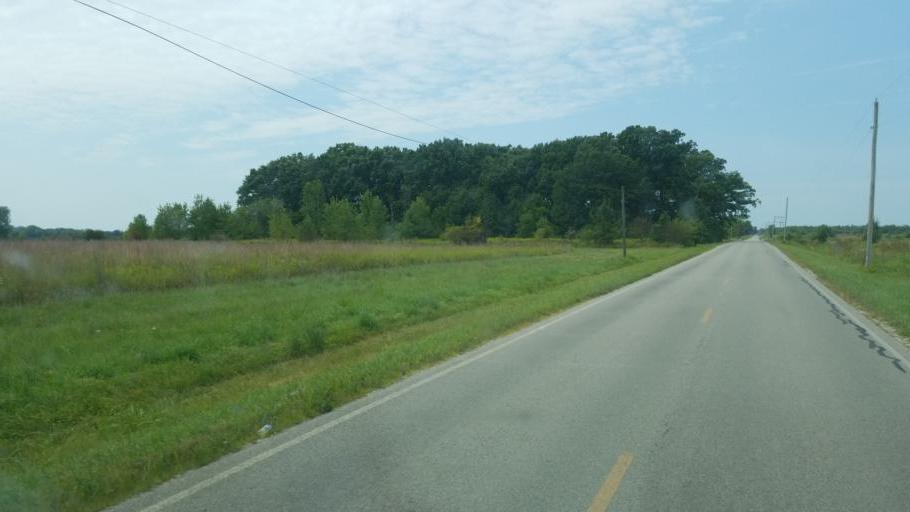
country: US
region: Ohio
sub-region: Marion County
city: Marion
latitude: 40.5713
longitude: -83.1748
